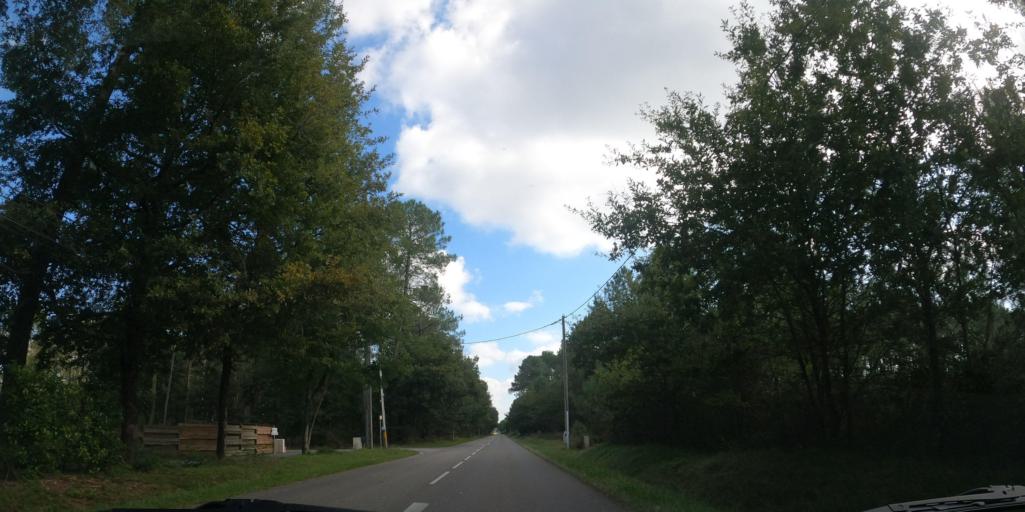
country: FR
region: Aquitaine
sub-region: Departement des Landes
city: Soustons
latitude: 43.7360
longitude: -1.2932
